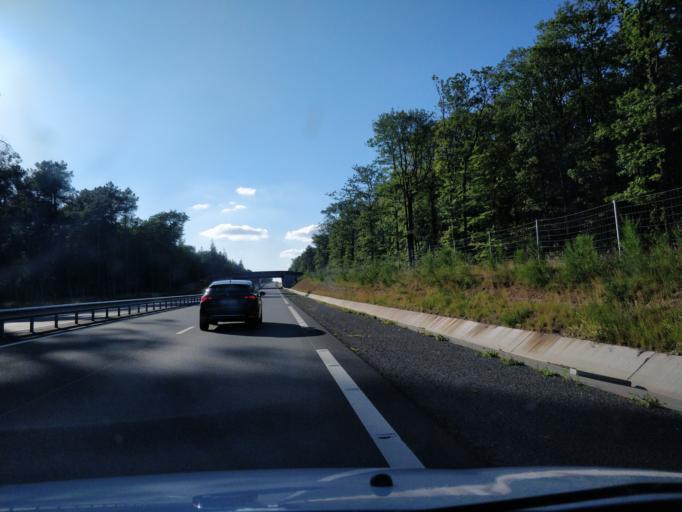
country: FR
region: Pays de la Loire
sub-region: Departement de la Loire-Atlantique
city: Soudan
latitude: 47.7883
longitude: -1.2595
